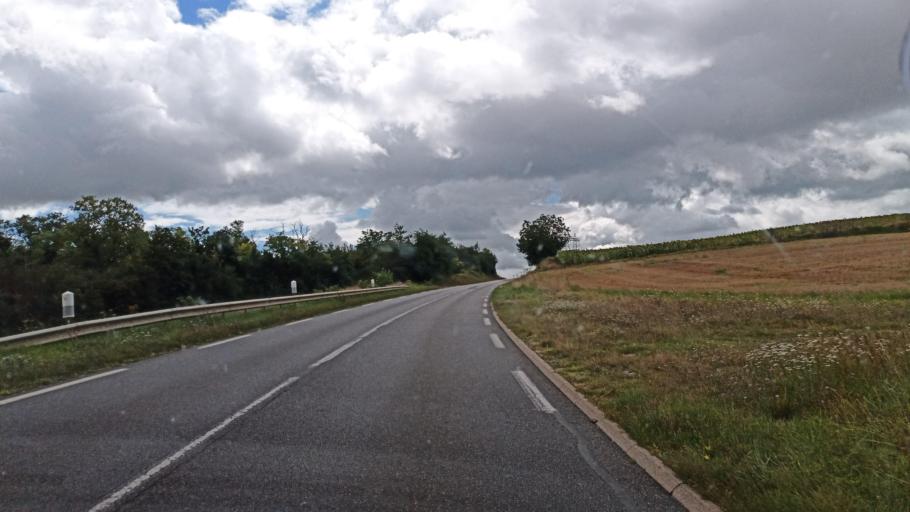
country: FR
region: Ile-de-France
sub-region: Departement de Seine-et-Marne
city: Cannes-Ecluse
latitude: 48.3343
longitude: 2.9582
